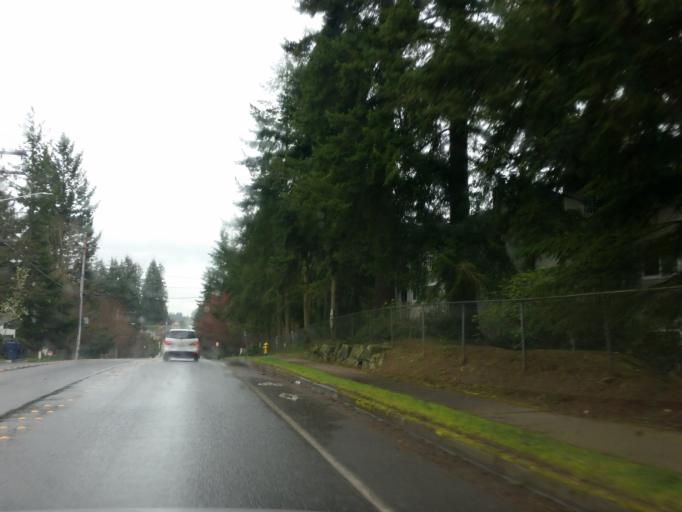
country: US
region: Washington
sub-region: Snohomish County
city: Lynnwood
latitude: 47.8175
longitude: -122.3124
